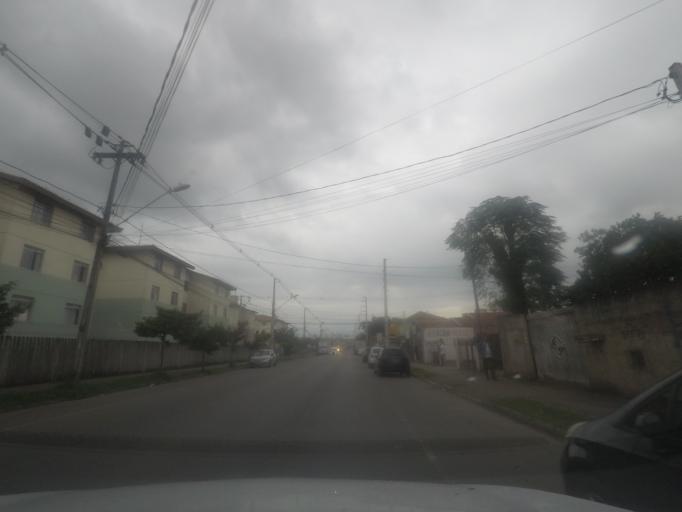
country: BR
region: Parana
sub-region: Sao Jose Dos Pinhais
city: Sao Jose dos Pinhais
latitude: -25.5540
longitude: -49.2516
